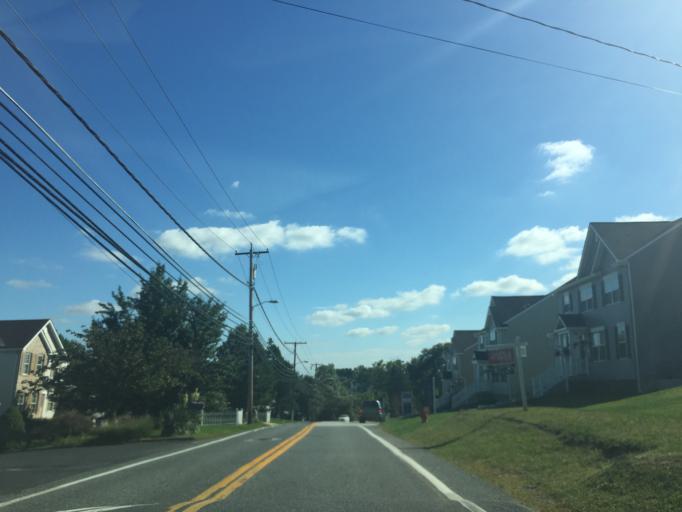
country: US
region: Maryland
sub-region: Baltimore County
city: Overlea
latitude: 39.3708
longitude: -76.4993
